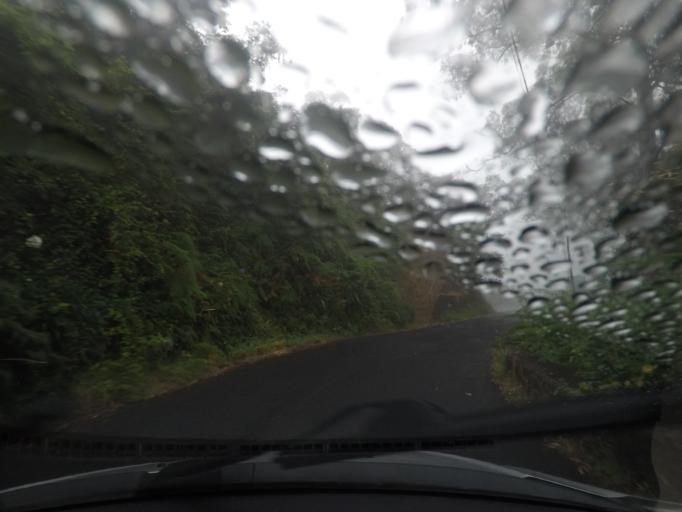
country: PT
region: Madeira
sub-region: Santana
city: Santana
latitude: 32.7562
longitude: -16.8684
